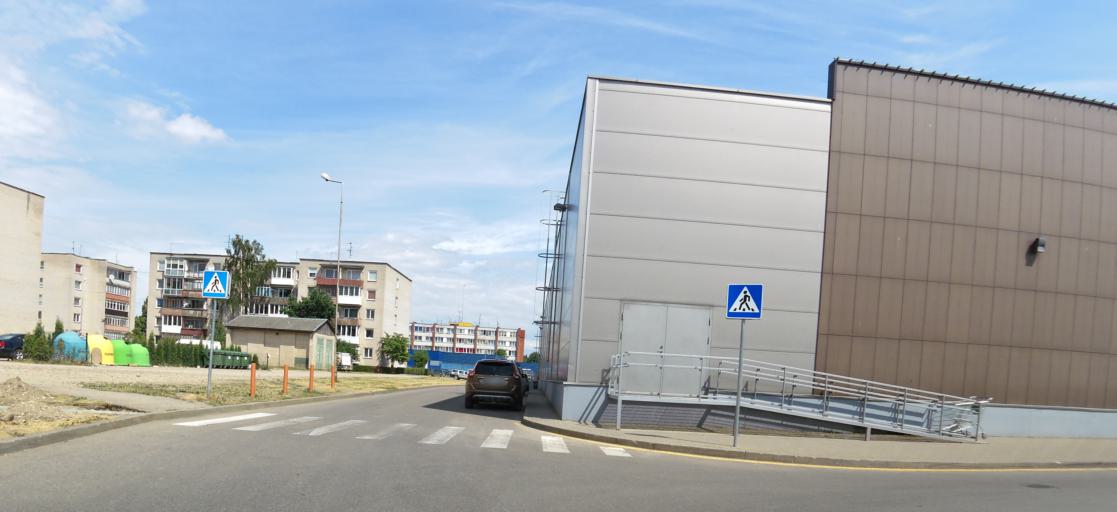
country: LT
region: Vilnius County
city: Ukmerge
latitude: 55.2431
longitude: 24.7434
